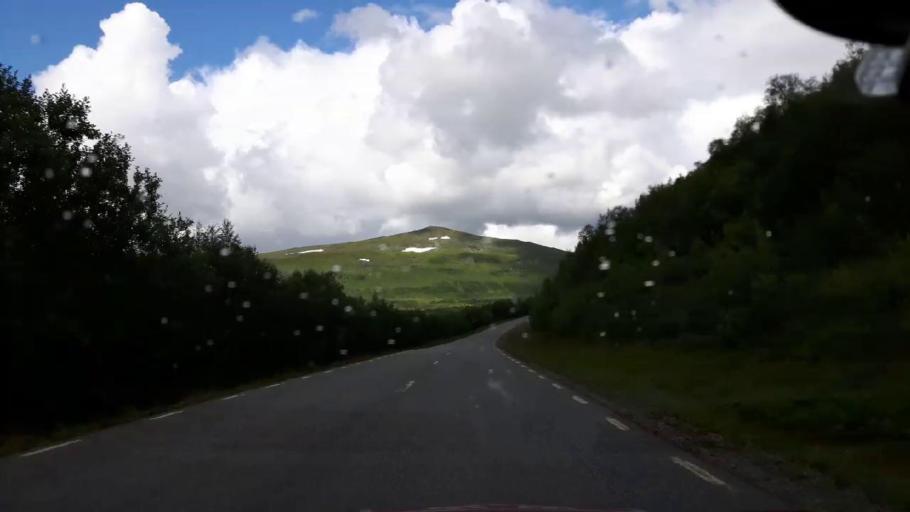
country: NO
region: Nordland
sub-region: Hattfjelldal
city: Hattfjelldal
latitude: 65.0693
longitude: 14.6622
